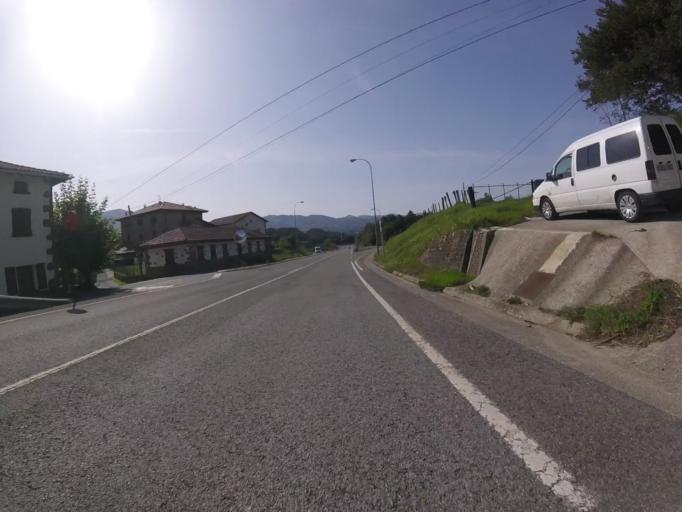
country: ES
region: Navarre
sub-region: Provincia de Navarra
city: Zugarramurdi
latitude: 43.1971
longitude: -1.4838
